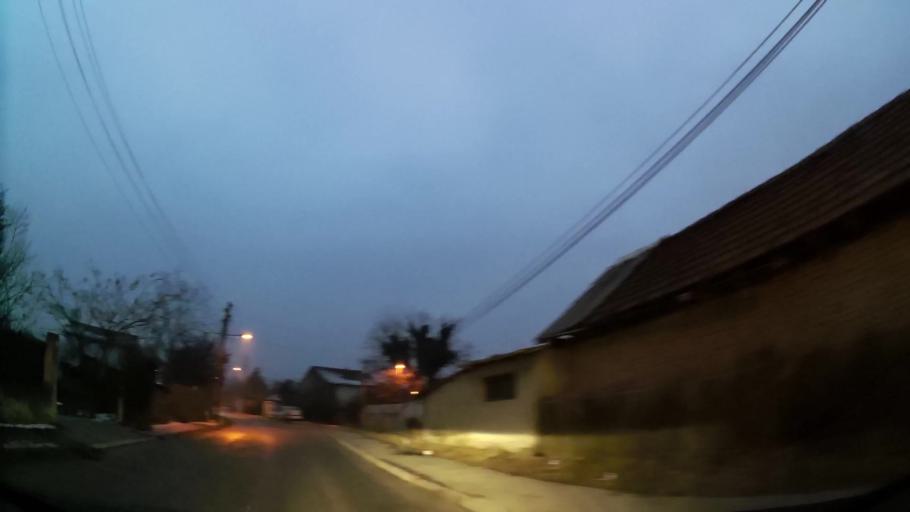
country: MK
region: Kisela Voda
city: Kisela Voda
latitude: 41.9656
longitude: 21.4853
